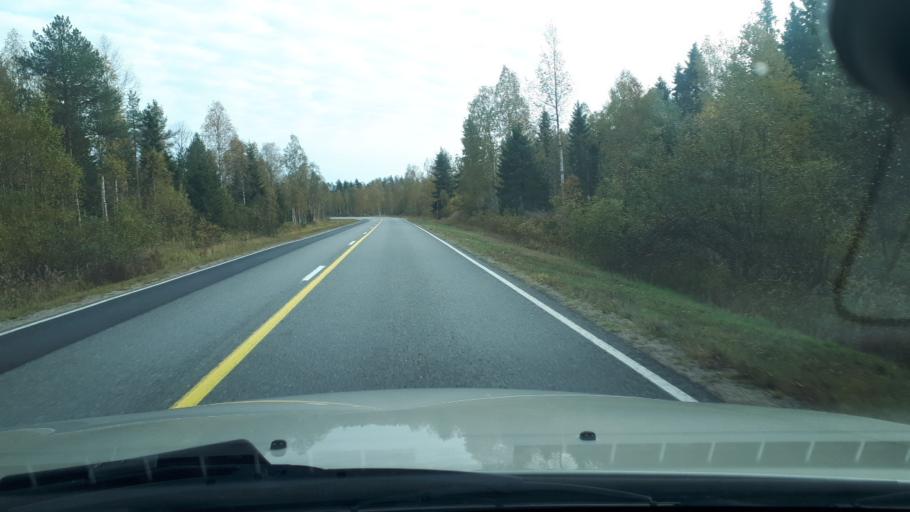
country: FI
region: Lapland
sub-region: Rovaniemi
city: Ranua
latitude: 65.9609
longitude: 26.0601
